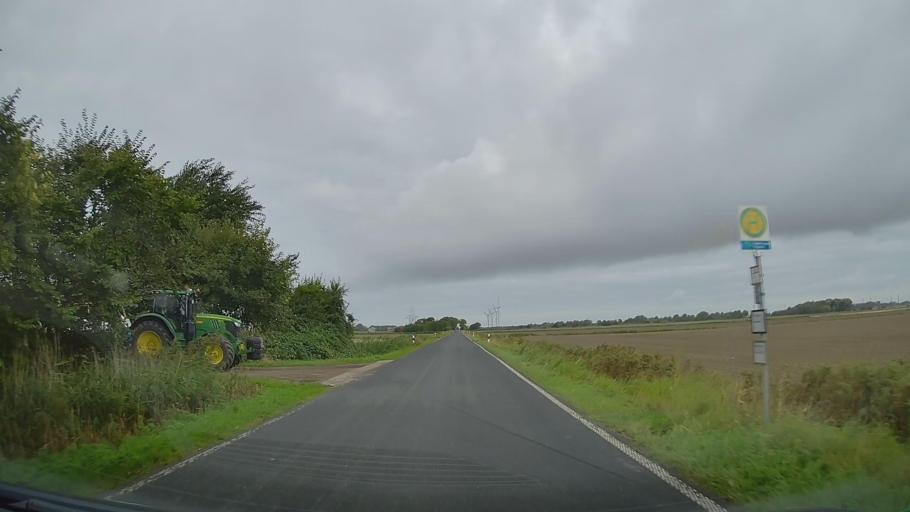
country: DE
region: Schleswig-Holstein
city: Galmsbull
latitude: 54.7565
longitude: 8.7261
